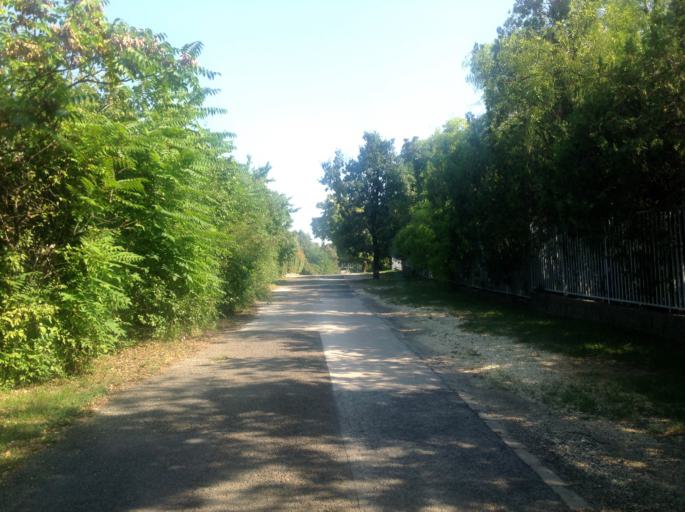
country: HU
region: Budapest
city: Budapest XII. keruelet
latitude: 47.4918
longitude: 18.9823
